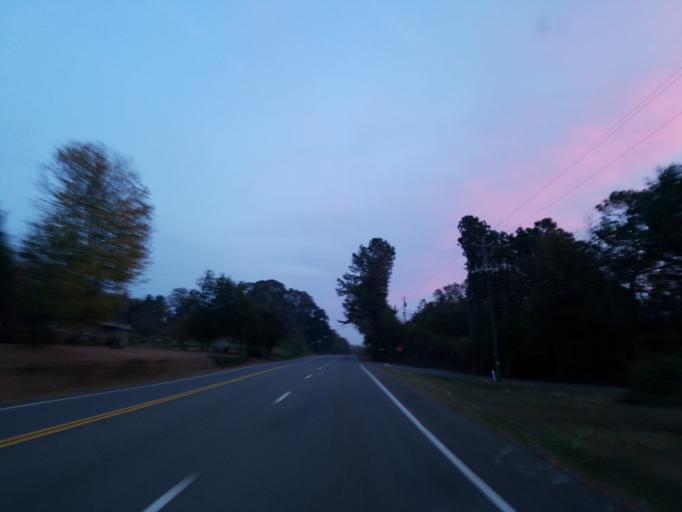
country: US
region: Georgia
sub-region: Pickens County
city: Jasper
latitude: 34.4915
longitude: -84.4626
